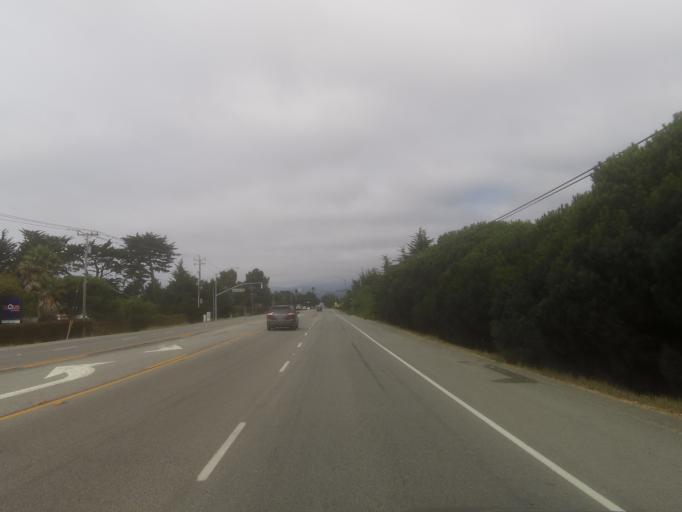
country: US
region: California
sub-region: San Mateo County
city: Half Moon Bay
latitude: 37.4337
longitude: -122.4268
